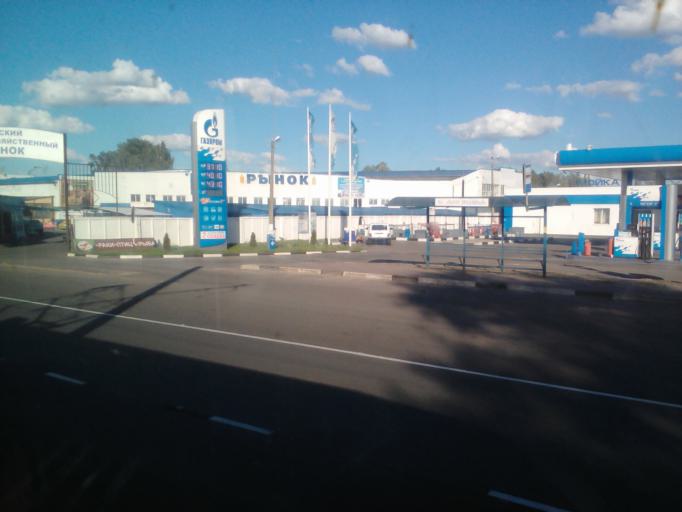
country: RU
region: Kursk
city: Kursk
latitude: 51.7080
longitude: 36.1799
